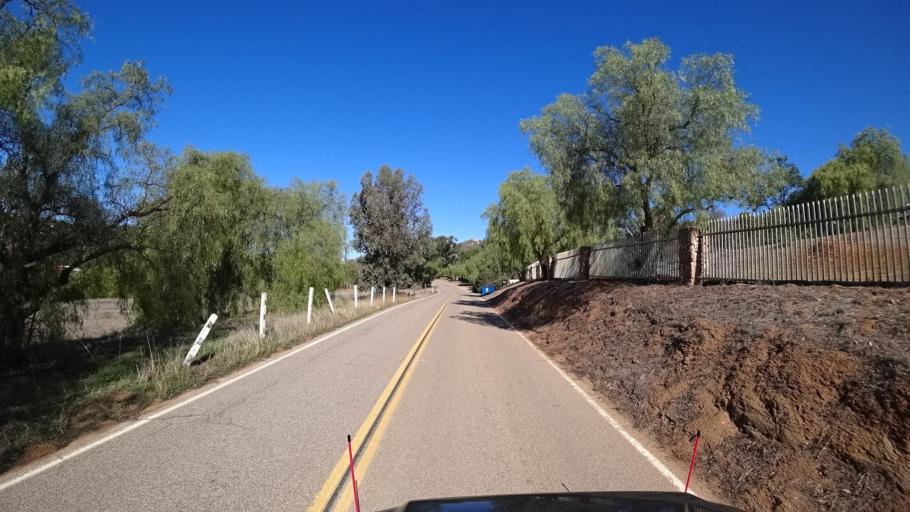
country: US
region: California
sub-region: San Diego County
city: Jamul
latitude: 32.7199
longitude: -116.8041
